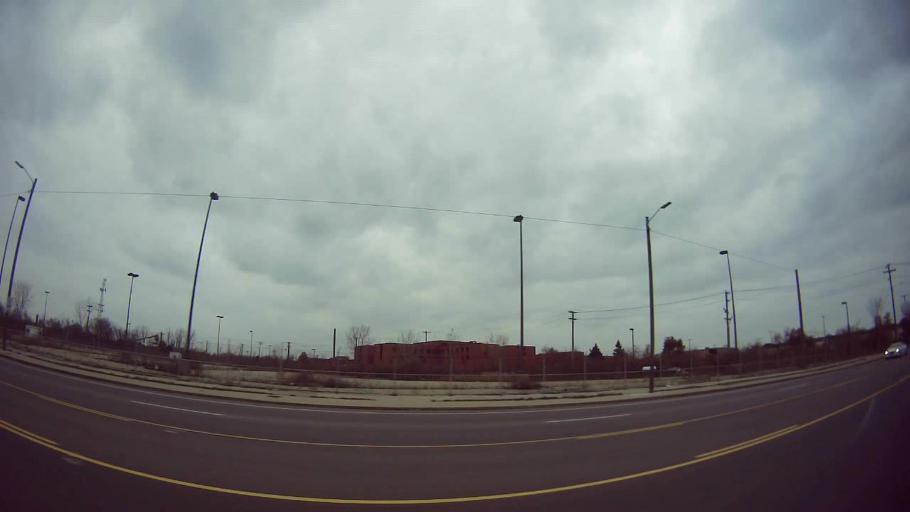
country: US
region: Michigan
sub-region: Wayne County
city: Grosse Pointe Park
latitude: 42.3881
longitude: -82.9813
